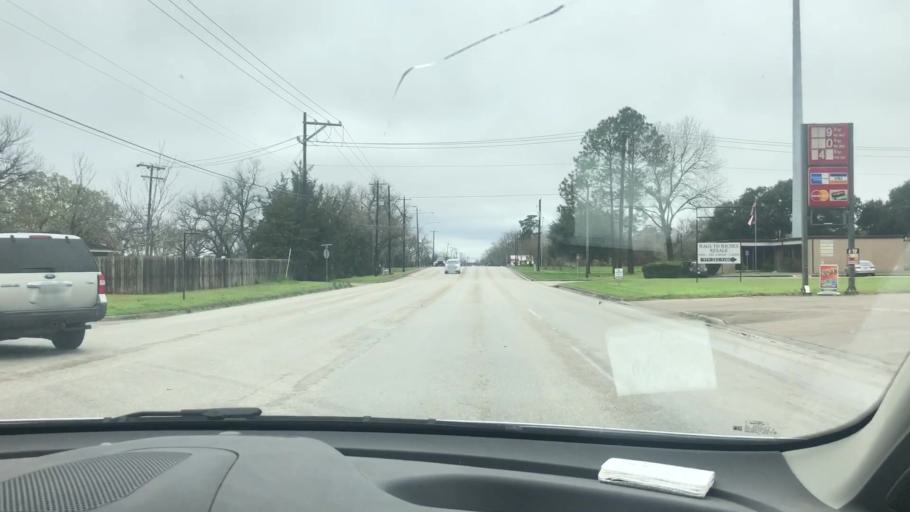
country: US
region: Texas
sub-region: Wharton County
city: Wharton
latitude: 29.3165
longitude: -96.0868
